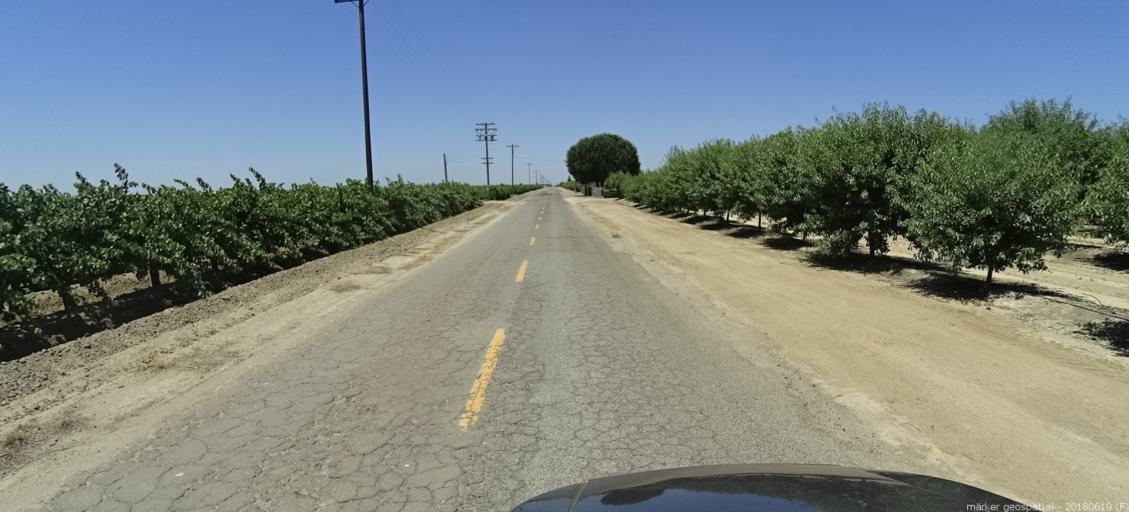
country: US
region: California
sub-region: Madera County
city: Parkwood
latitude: 36.8657
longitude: -120.1320
